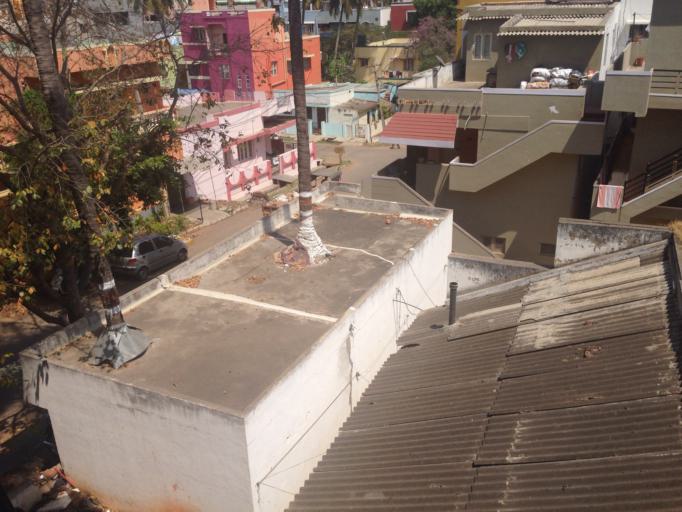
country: IN
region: Karnataka
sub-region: Mysore
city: Mysore
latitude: 12.3293
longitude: 76.6287
